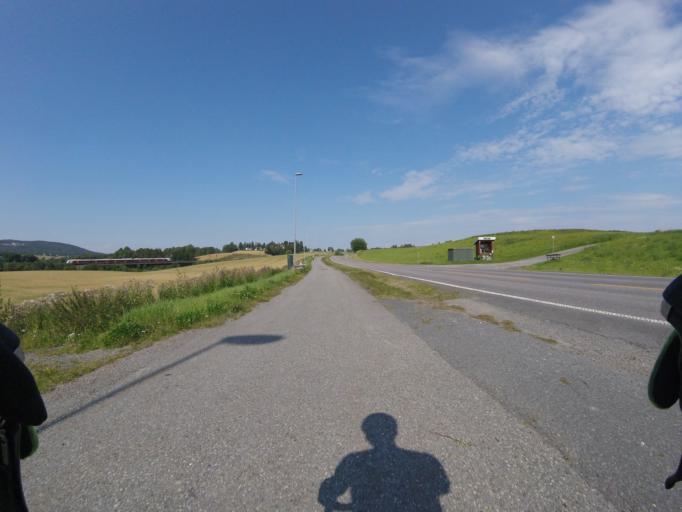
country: NO
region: Akershus
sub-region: Sorum
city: Frogner
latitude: 60.0096
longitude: 11.1087
